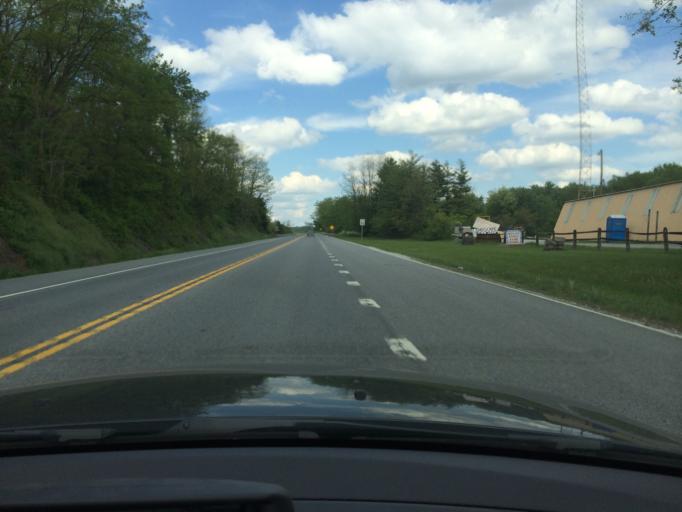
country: US
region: Maryland
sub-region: Carroll County
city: New Windsor
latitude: 39.5497
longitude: -77.0551
